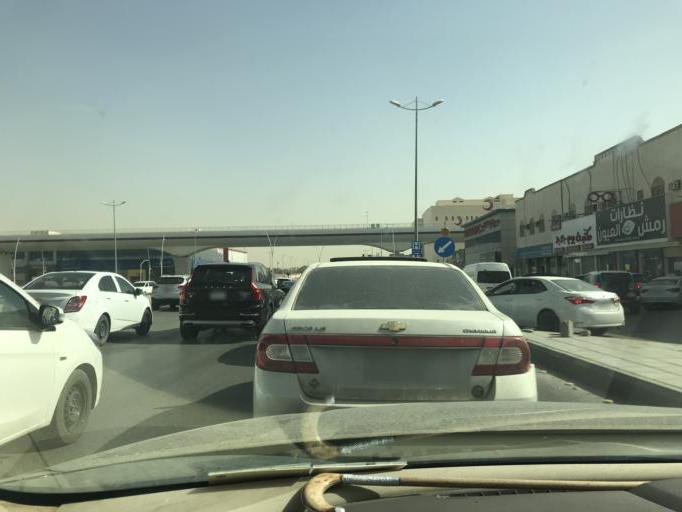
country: SA
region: Ar Riyad
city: Riyadh
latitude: 24.7939
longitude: 46.7433
